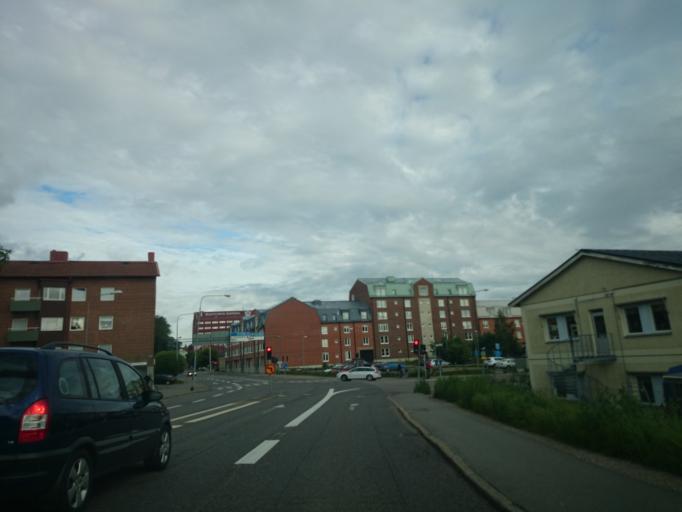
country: SE
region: Vaesternorrland
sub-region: Sundsvalls Kommun
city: Sundsvall
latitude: 62.3852
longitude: 17.3124
